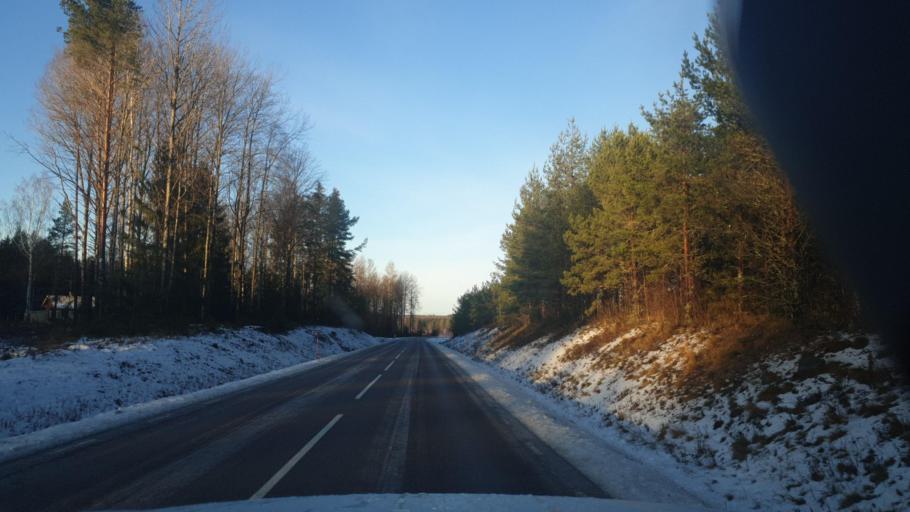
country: SE
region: Vaermland
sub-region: Arvika Kommun
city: Arvika
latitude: 59.5179
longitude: 12.6299
